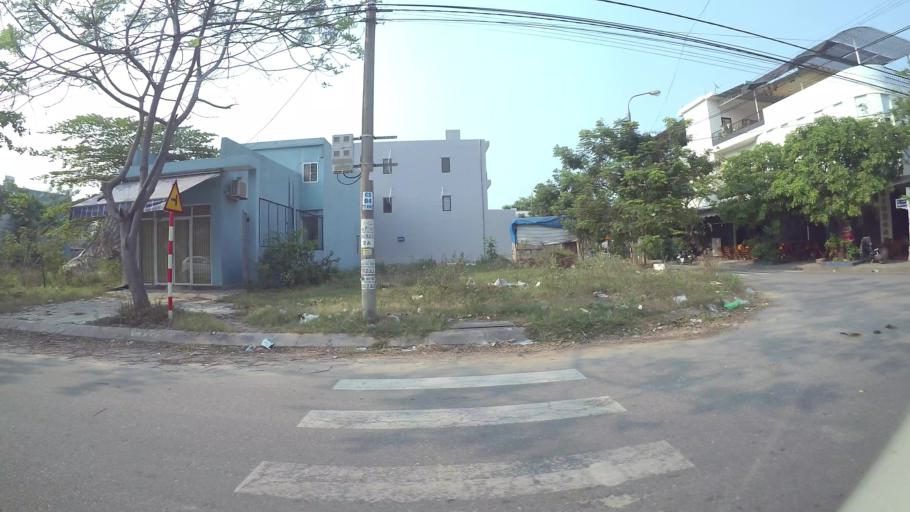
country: VN
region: Da Nang
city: Lien Chieu
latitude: 16.0533
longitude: 108.1658
